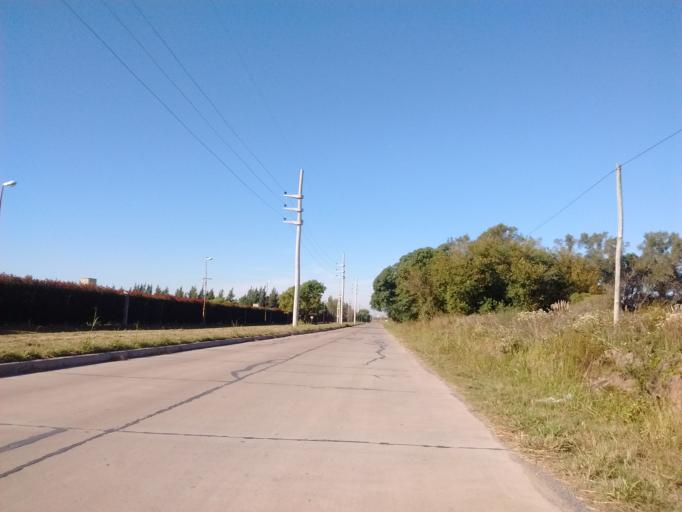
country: AR
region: Santa Fe
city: Funes
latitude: -32.9357
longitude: -60.8119
